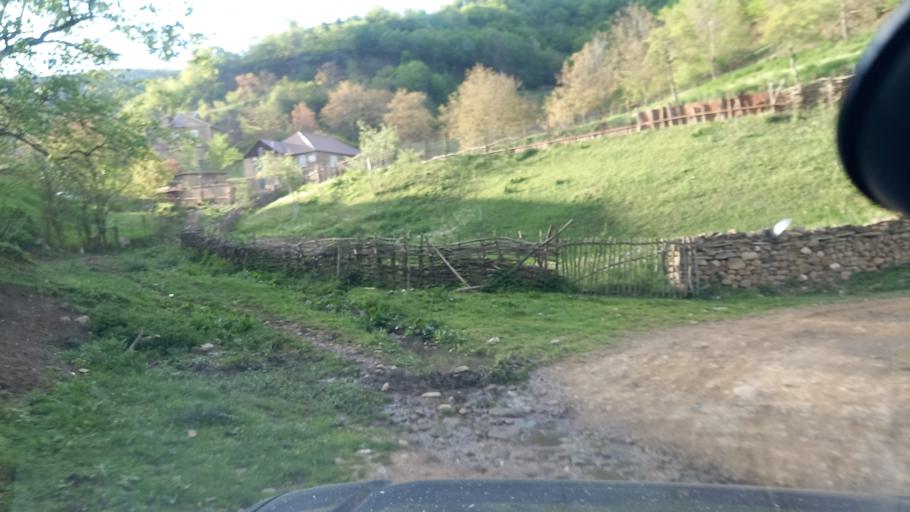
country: RU
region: Dagestan
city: Khuchni
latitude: 41.9472
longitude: 47.8326
